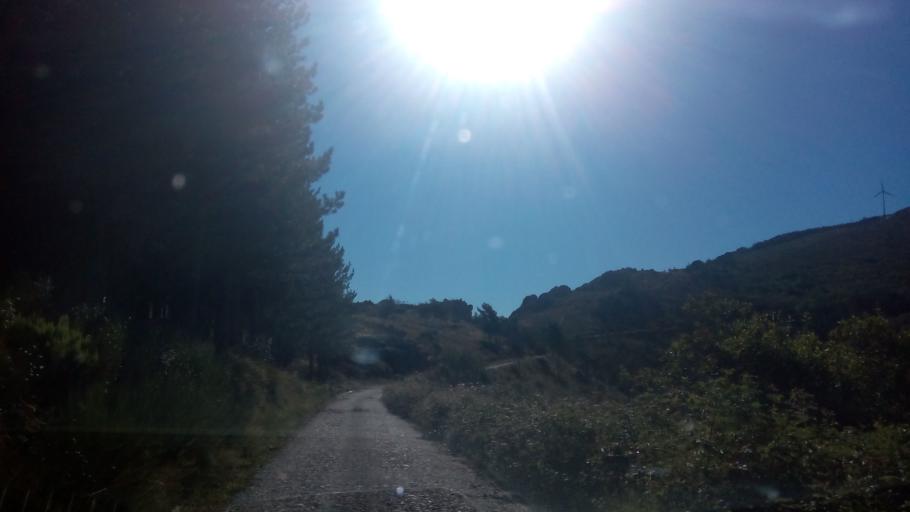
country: PT
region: Vila Real
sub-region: Mesao Frio
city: Mesao Frio
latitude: 41.2722
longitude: -7.9119
